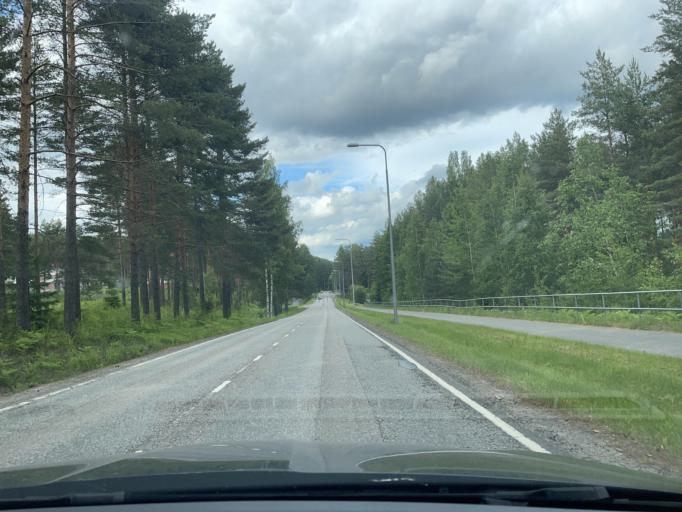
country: FI
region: Central Finland
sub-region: Jaemsae
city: Jaemsaenkoski
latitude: 61.9170
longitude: 25.1478
